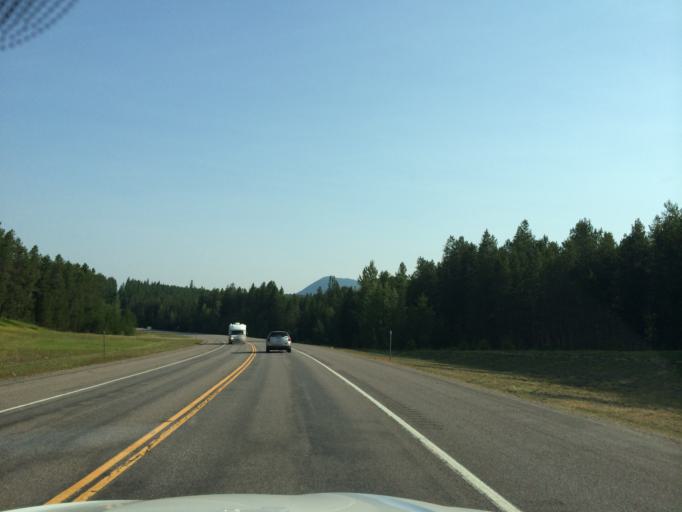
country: US
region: Montana
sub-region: Flathead County
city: Columbia Falls
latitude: 48.4667
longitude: -113.9970
